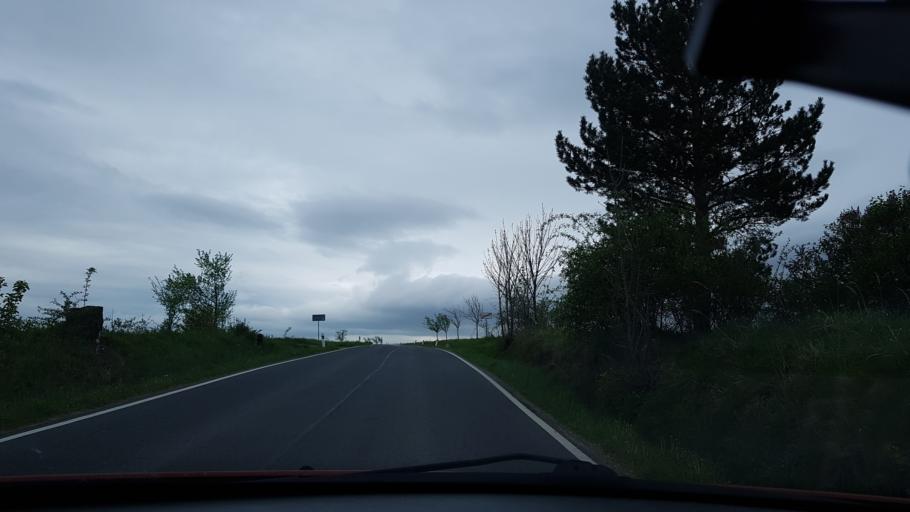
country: CZ
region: Olomoucky
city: Javornik
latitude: 50.4075
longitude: 16.9902
